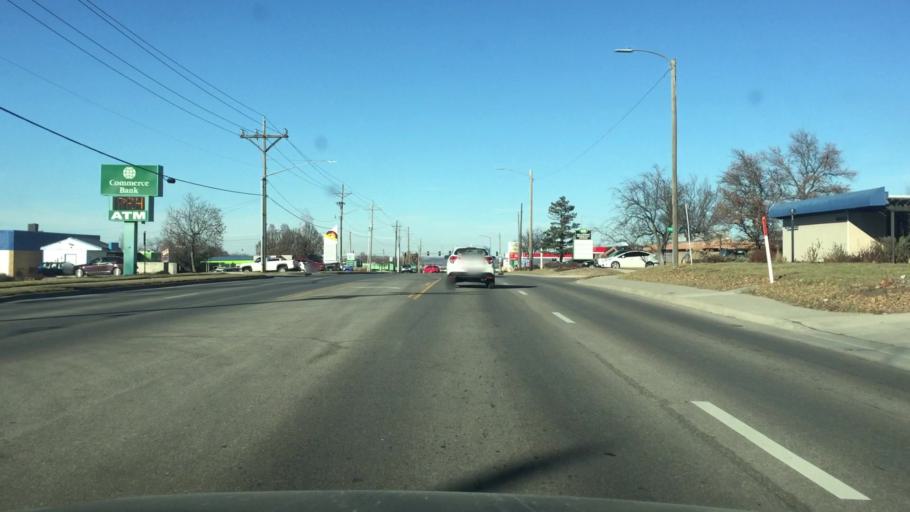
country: US
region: Kansas
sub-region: Douglas County
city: Lawrence
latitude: 38.9654
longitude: -95.2604
